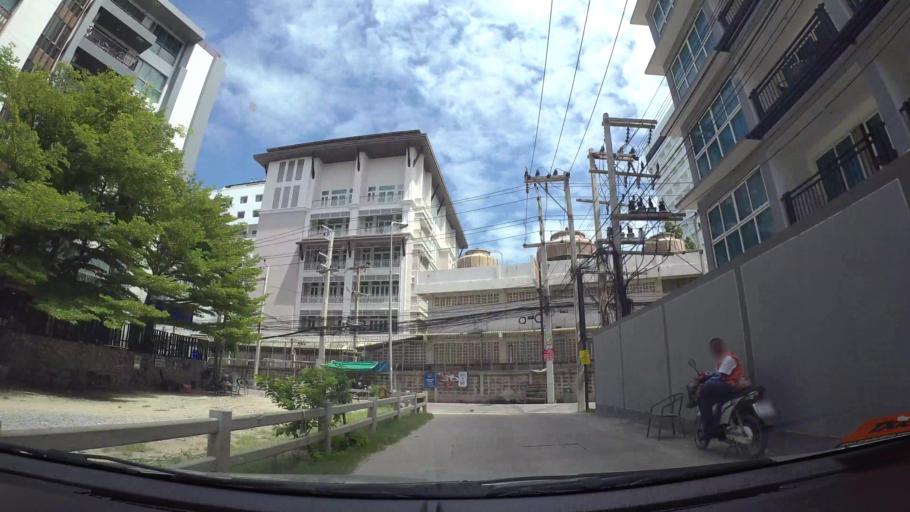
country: TH
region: Chon Buri
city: Phatthaya
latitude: 12.9275
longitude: 100.8803
